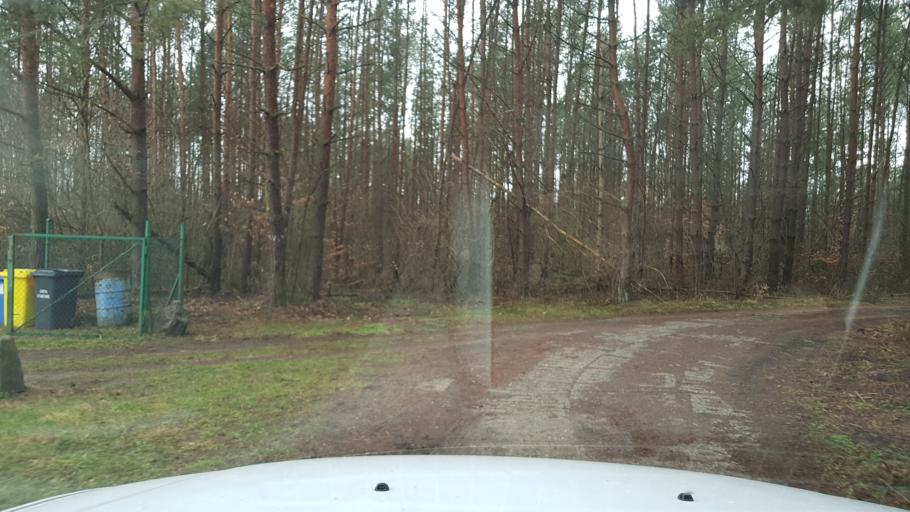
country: PL
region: West Pomeranian Voivodeship
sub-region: Powiat drawski
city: Czaplinek
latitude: 53.5742
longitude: 16.2490
